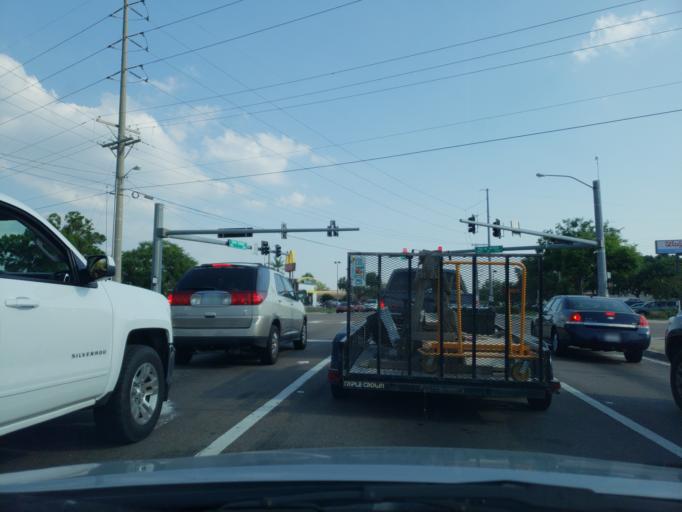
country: US
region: Florida
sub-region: Hillsborough County
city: Palm River-Clair Mel
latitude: 27.9413
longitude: -82.3688
